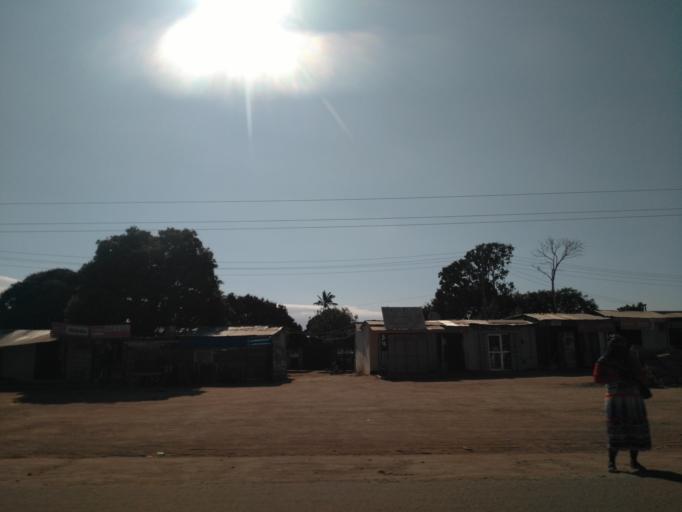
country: TZ
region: Dodoma
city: Dodoma
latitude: -6.1212
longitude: 35.7465
